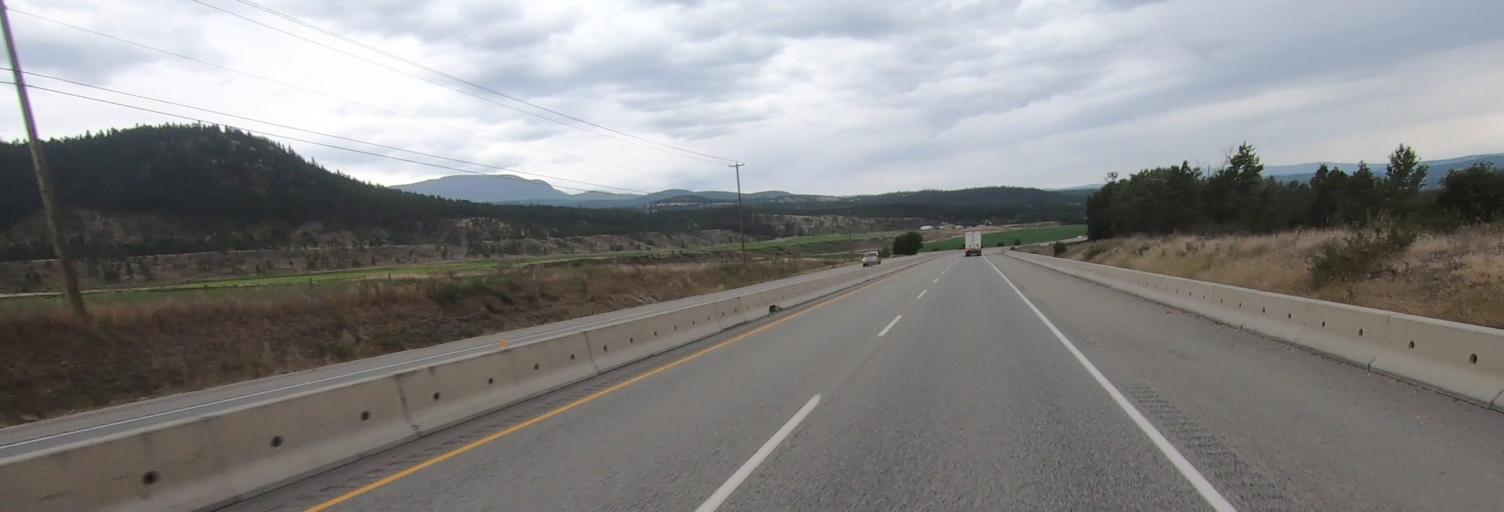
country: CA
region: British Columbia
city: Chase
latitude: 50.7080
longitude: -119.7916
